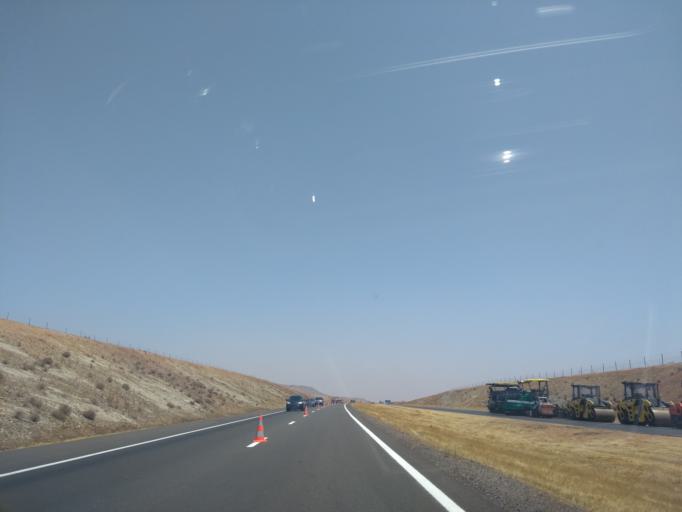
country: MA
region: Marrakech-Tensift-Al Haouz
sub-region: Kelaa-Des-Sraghna
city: Sidi Abdallah
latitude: 32.4400
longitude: -7.9318
